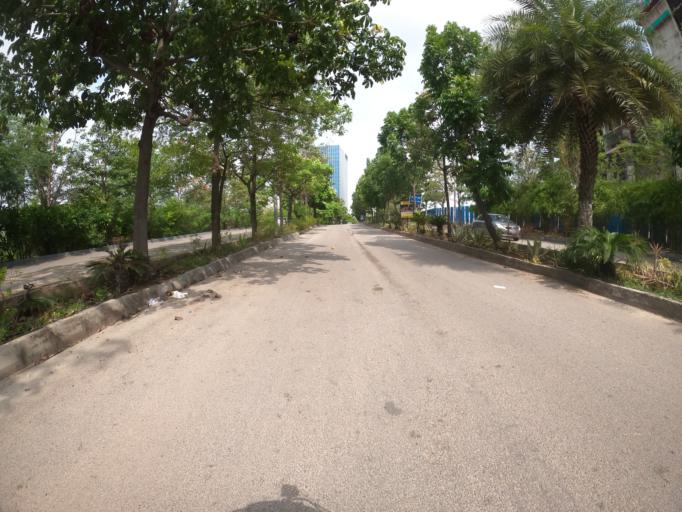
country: IN
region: Telangana
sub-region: Rangareddi
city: Kukatpalli
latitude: 17.4129
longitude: 78.3681
